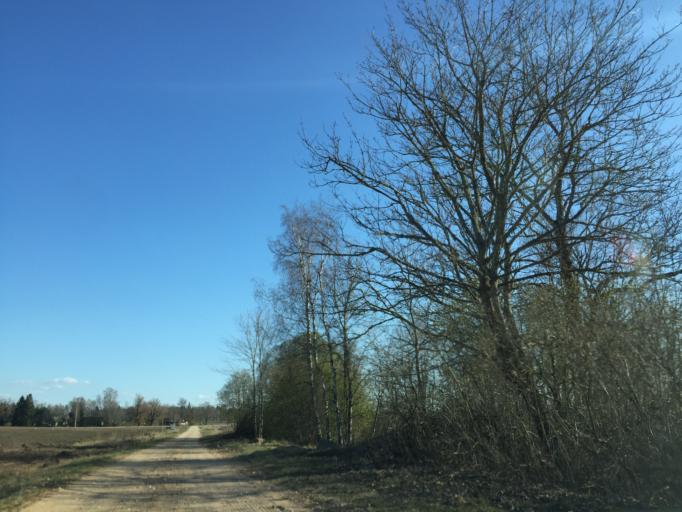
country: EE
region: Valgamaa
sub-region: Torva linn
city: Torva
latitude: 58.2399
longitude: 25.9272
